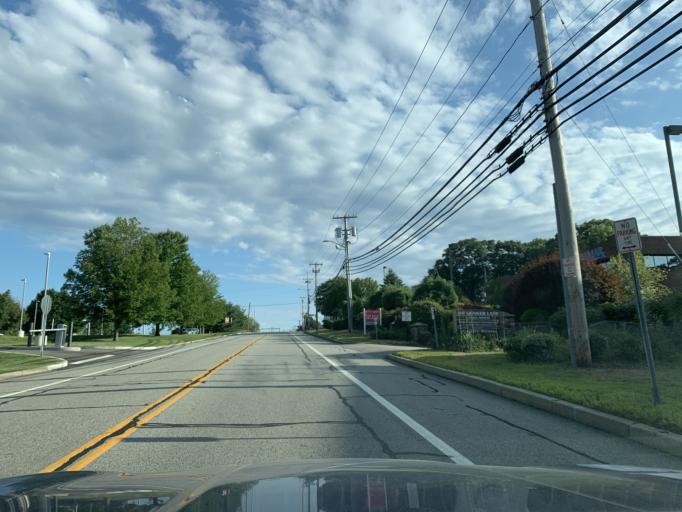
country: US
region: Rhode Island
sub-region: Kent County
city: West Warwick
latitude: 41.6911
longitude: -71.5012
